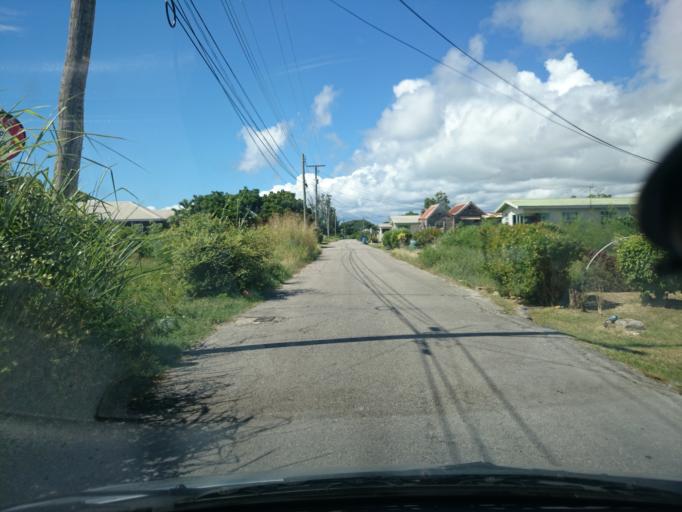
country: BB
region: Christ Church
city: Oistins
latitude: 13.0508
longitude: -59.5235
